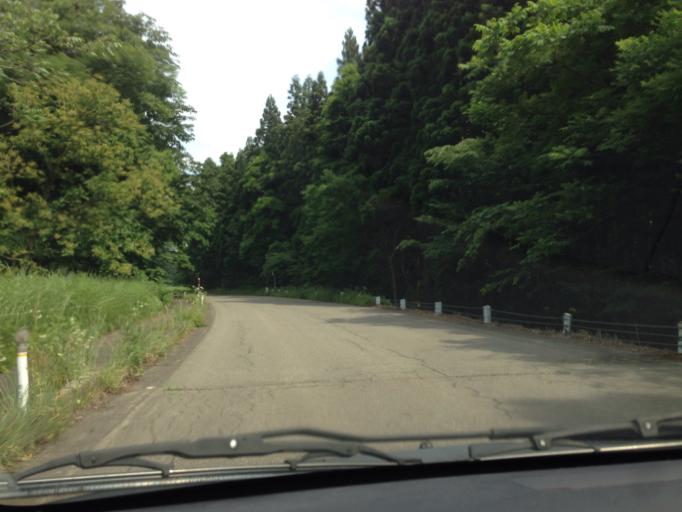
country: JP
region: Fukushima
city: Kitakata
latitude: 37.5288
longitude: 139.7960
